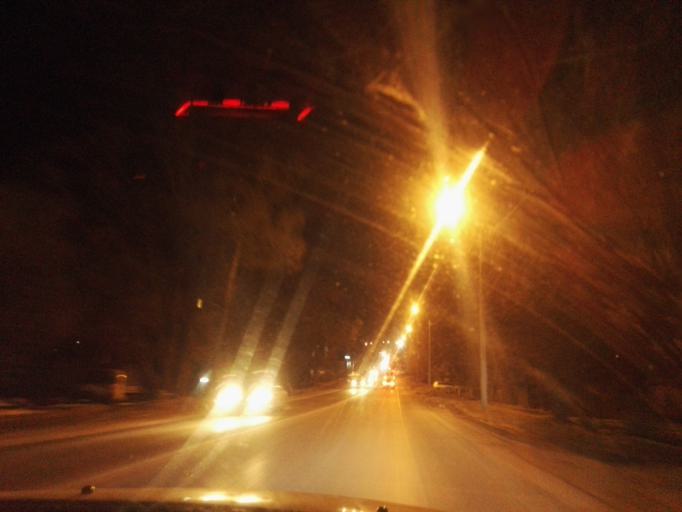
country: RU
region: Tula
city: Skuratovskiy
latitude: 54.1307
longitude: 37.6803
